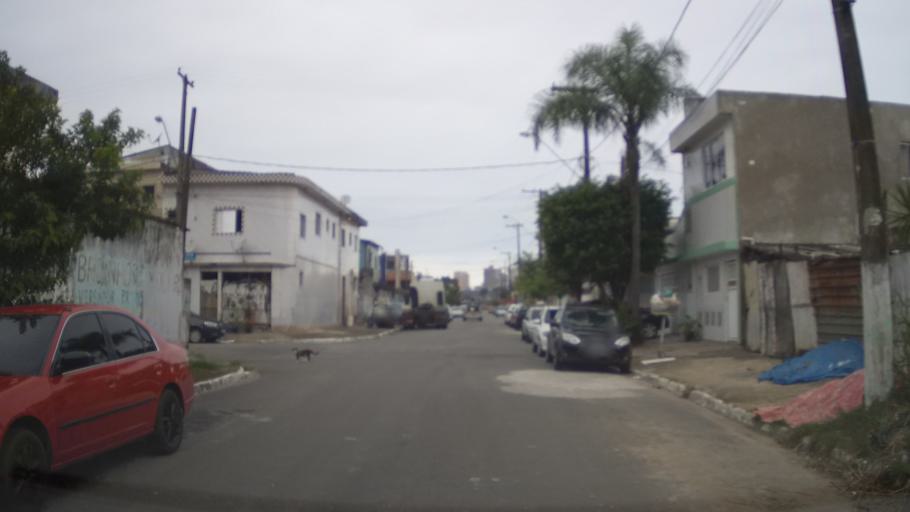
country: BR
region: Sao Paulo
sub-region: Praia Grande
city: Praia Grande
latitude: -23.9987
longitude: -46.4327
